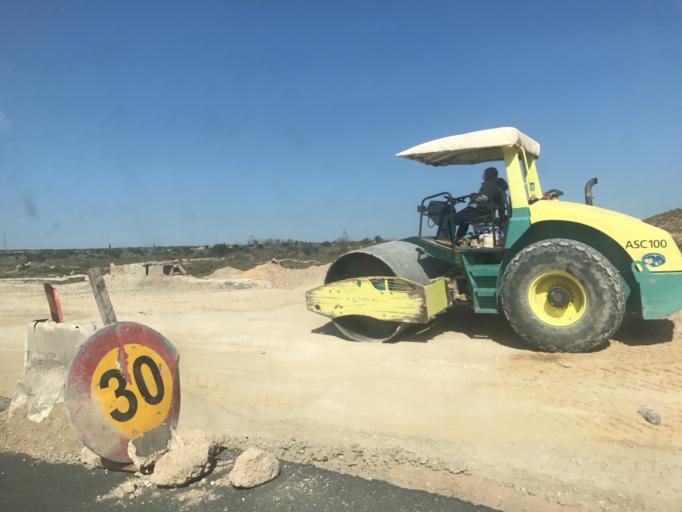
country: TN
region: Susah
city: Masakin
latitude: 35.7811
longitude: 10.5647
